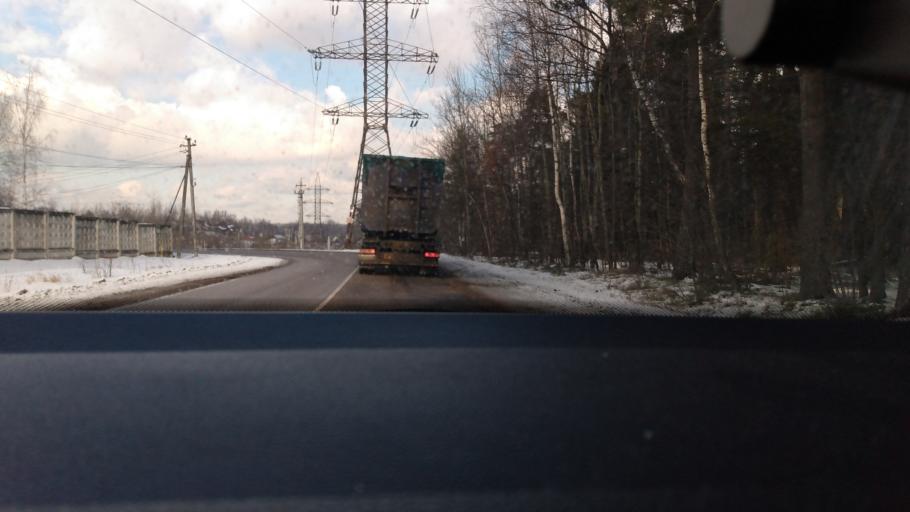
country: RU
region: Moskovskaya
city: Rodniki
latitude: 55.6881
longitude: 38.0817
